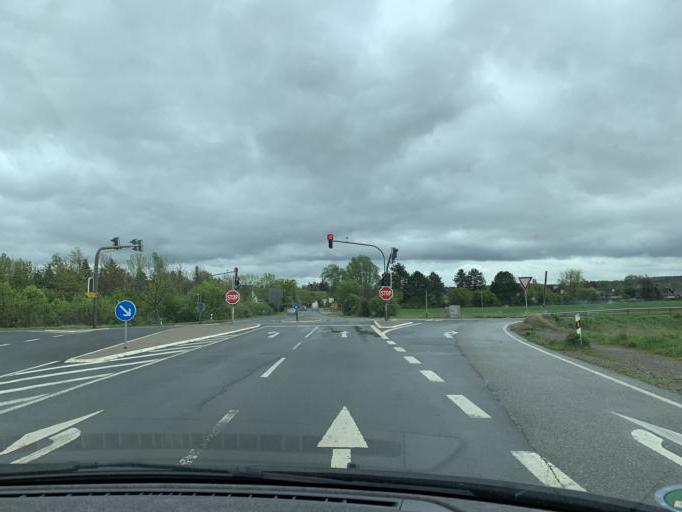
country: DE
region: North Rhine-Westphalia
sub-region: Regierungsbezirk Koln
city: Mechernich
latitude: 50.6416
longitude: 6.6972
